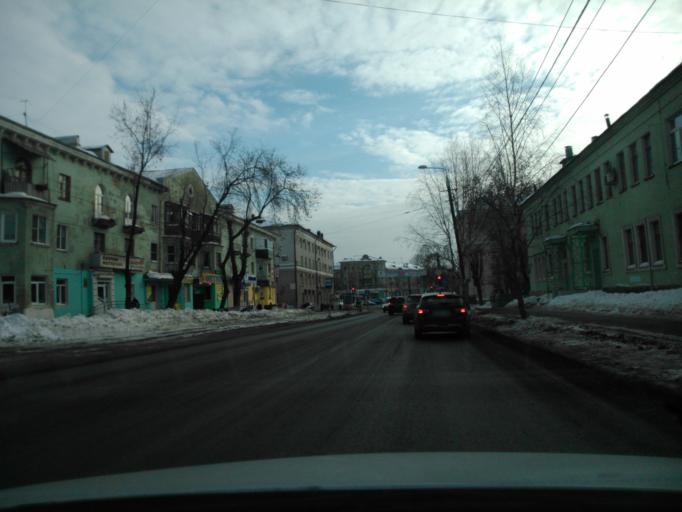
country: RU
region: Perm
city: Perm
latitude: 57.9950
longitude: 56.2463
